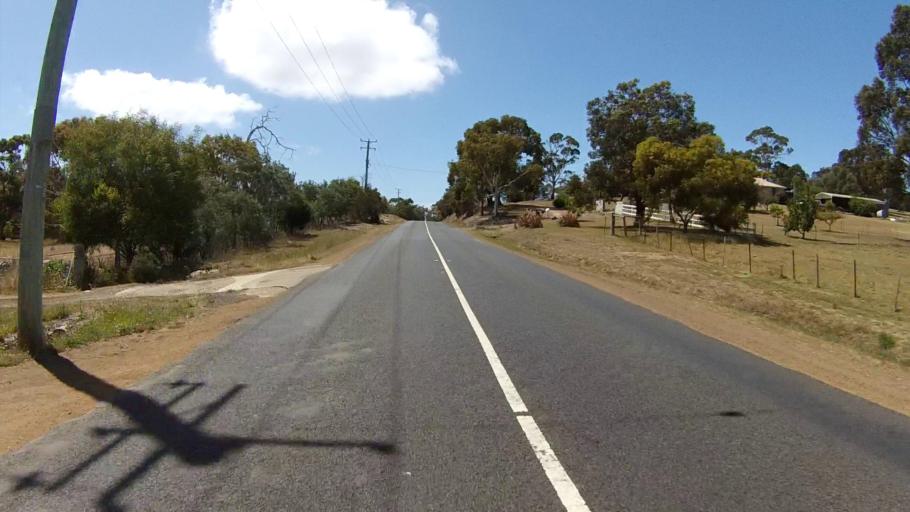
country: AU
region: Tasmania
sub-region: Clarence
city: Sandford
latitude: -42.9598
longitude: 147.4746
